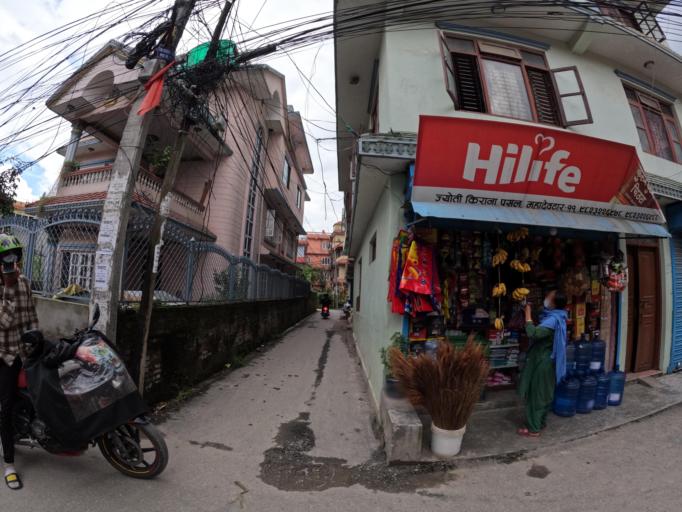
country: NP
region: Central Region
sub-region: Bagmati Zone
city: Kathmandu
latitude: 27.7441
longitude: 85.3195
